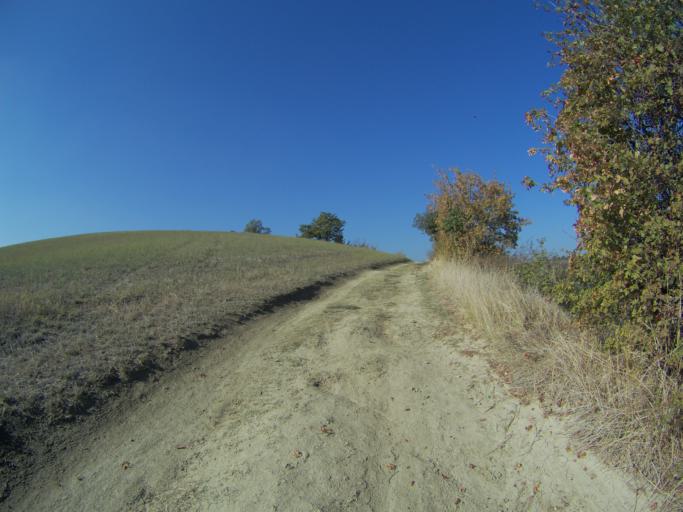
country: IT
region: Emilia-Romagna
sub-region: Provincia di Reggio Emilia
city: Vezzano sul Crostolo
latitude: 44.6125
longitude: 10.5435
